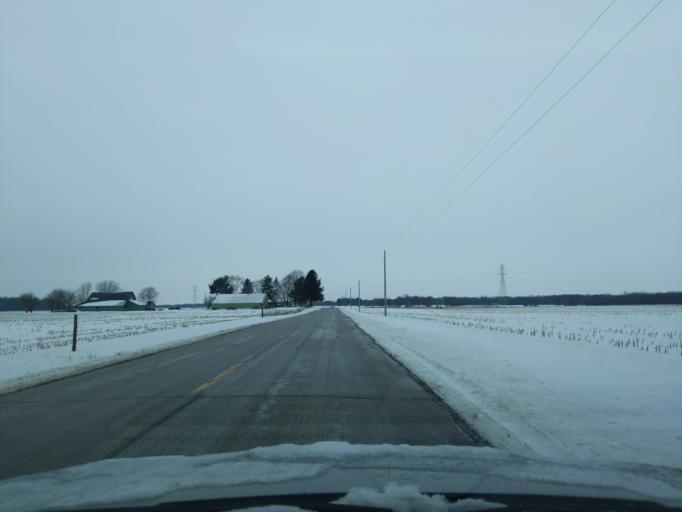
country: US
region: Indiana
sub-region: Benton County
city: Otterbein
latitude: 40.4169
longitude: -87.0807
